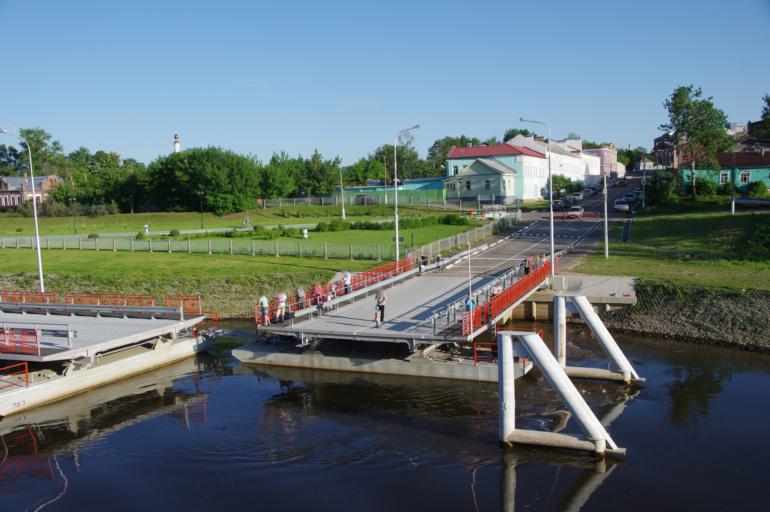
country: RU
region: Moskovskaya
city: Kolomna
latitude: 55.1082
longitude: 38.7640
